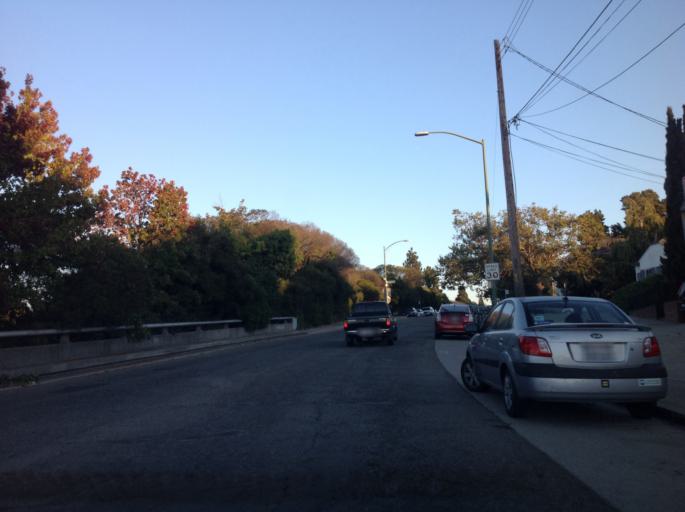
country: US
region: California
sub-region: Alameda County
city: Oakland
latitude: 37.8178
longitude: -122.2532
